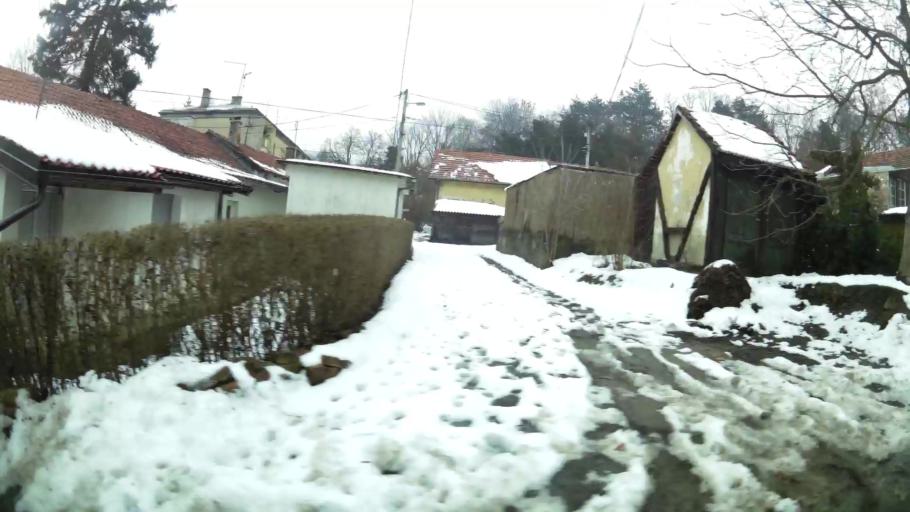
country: RS
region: Central Serbia
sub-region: Belgrade
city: Savski Venac
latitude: 44.7802
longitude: 20.4458
